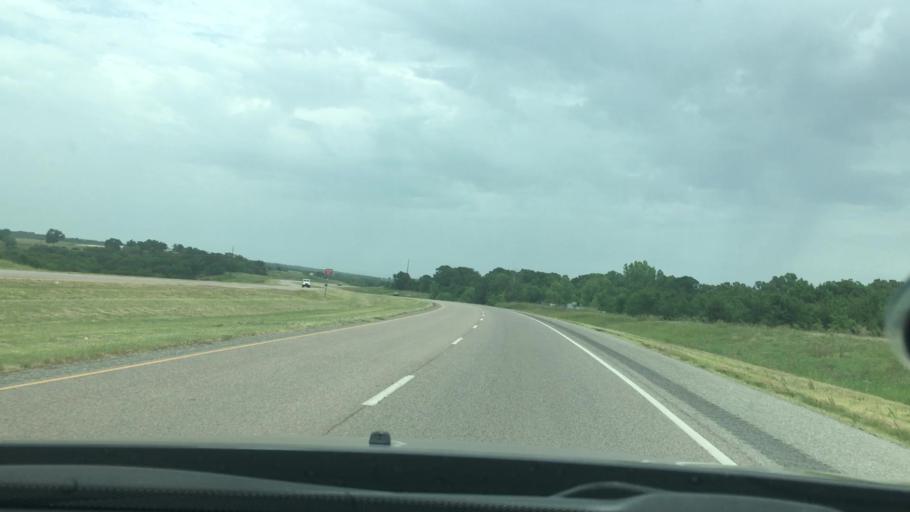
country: US
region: Oklahoma
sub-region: Pontotoc County
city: Ada
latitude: 34.8184
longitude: -96.6930
